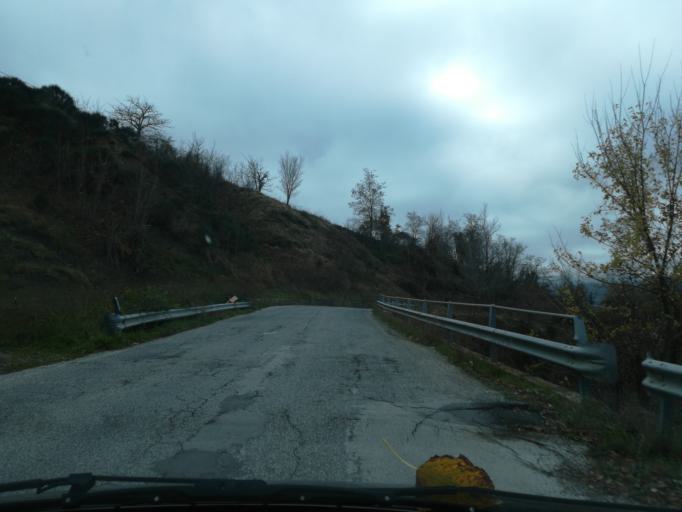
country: IT
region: Molise
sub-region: Provincia di Isernia
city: Agnone
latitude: 41.8190
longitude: 14.3731
